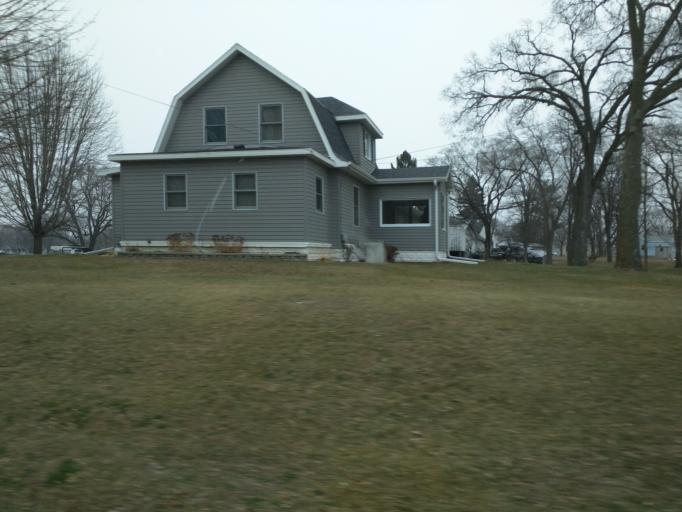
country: US
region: Wisconsin
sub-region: La Crosse County
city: French Island
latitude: 43.8465
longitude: -91.2652
